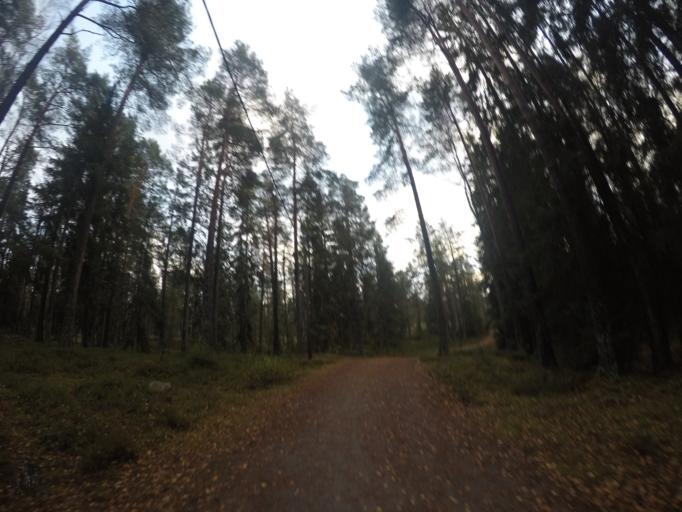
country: SE
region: Soedermanland
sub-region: Eskilstuna Kommun
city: Eskilstuna
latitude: 59.3464
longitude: 16.5260
